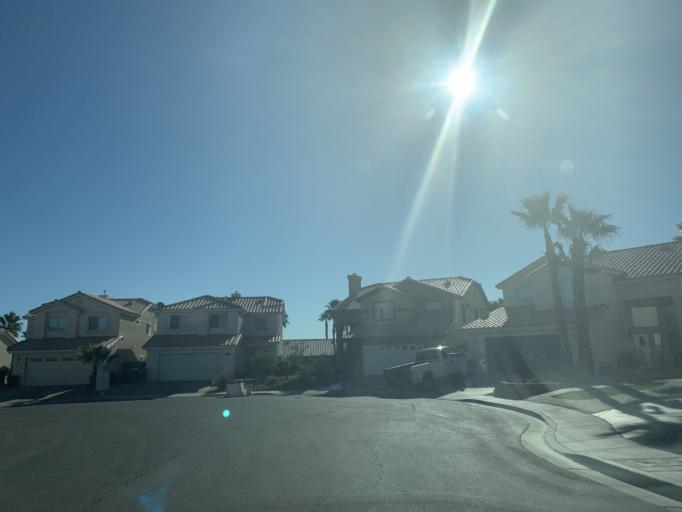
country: US
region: Nevada
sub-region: Clark County
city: Summerlin South
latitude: 36.1213
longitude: -115.3026
